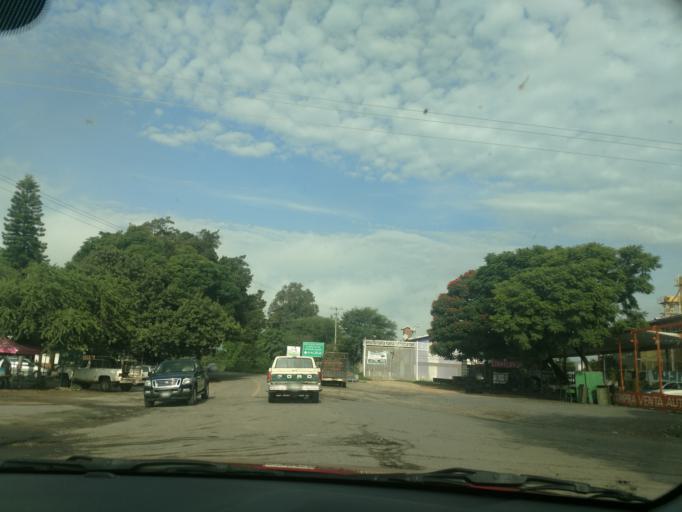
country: MX
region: Jalisco
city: Ameca
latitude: 20.5385
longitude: -104.0458
